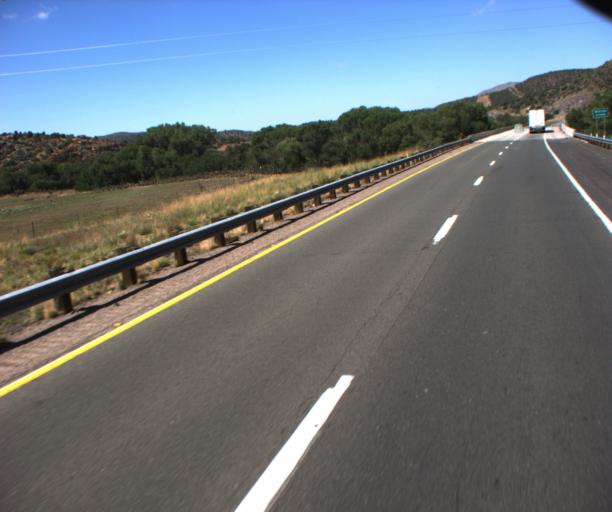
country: US
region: Arizona
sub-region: Mohave County
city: Peach Springs
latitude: 35.1845
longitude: -113.4604
